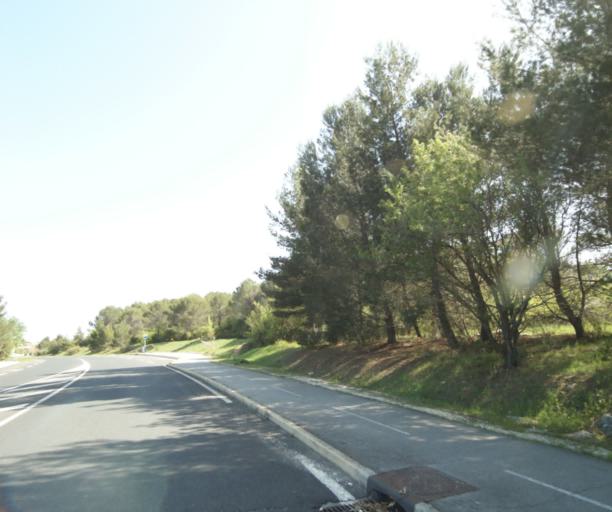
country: FR
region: Languedoc-Roussillon
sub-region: Departement de l'Herault
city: Grabels
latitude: 43.6434
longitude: 3.8236
